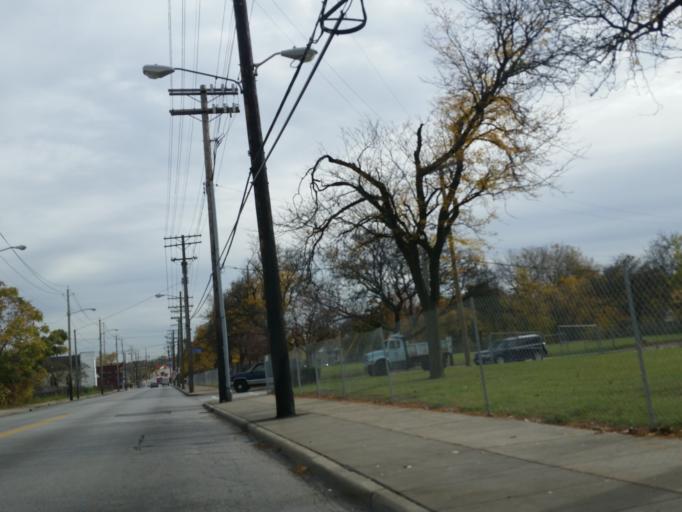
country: US
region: Ohio
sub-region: Cuyahoga County
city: Newburgh Heights
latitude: 41.4781
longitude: -81.6353
